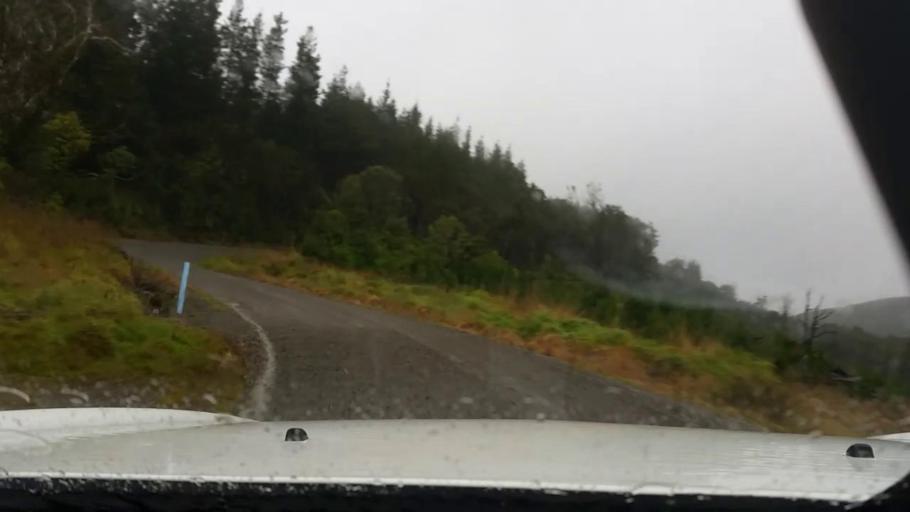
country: NZ
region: Wellington
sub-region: Masterton District
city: Masterton
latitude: -41.1832
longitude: 175.8238
